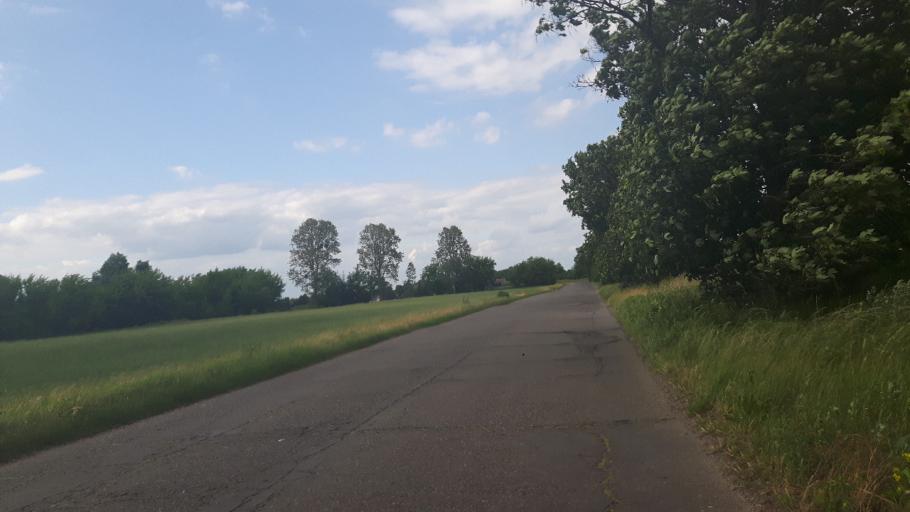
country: DE
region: Brandenburg
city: Rudnitz
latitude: 52.6931
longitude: 13.6604
